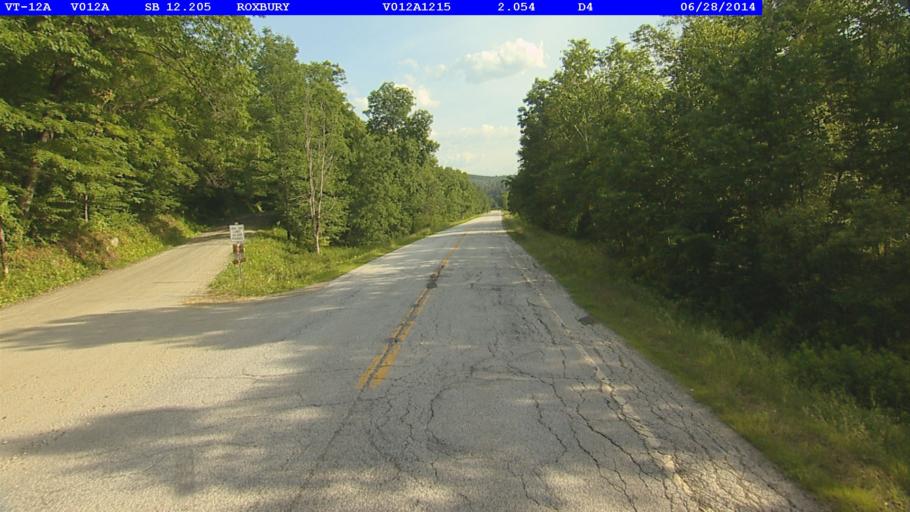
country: US
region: Vermont
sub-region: Washington County
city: Northfield
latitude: 44.0581
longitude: -72.7427
